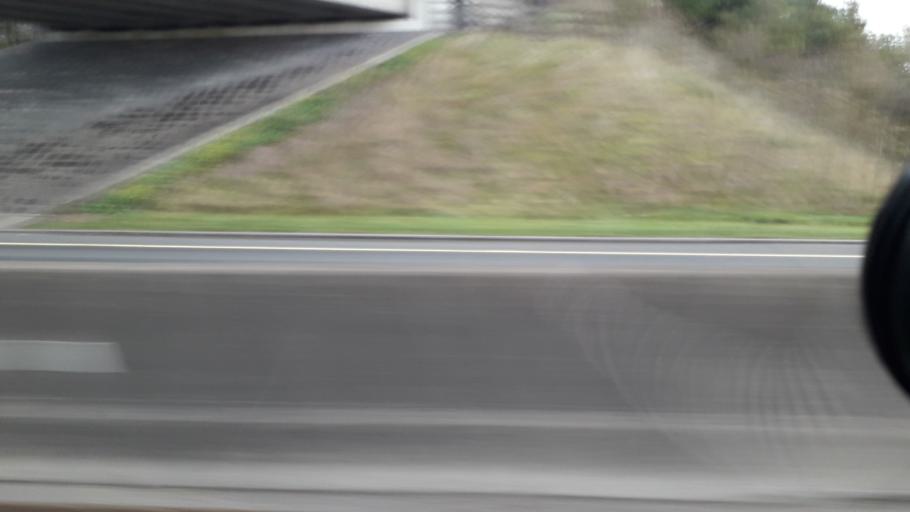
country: IE
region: Leinster
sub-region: An Mhi
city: Ashbourne
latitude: 53.4966
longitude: -6.4163
